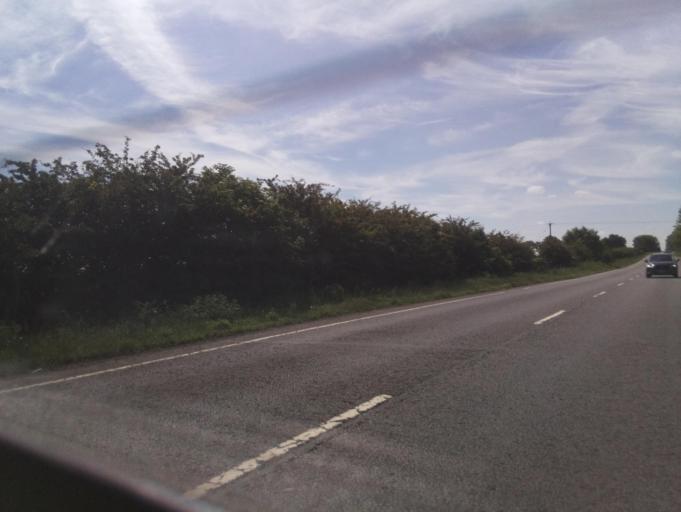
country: GB
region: England
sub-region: Lincolnshire
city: Burton
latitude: 53.3421
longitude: -0.5442
